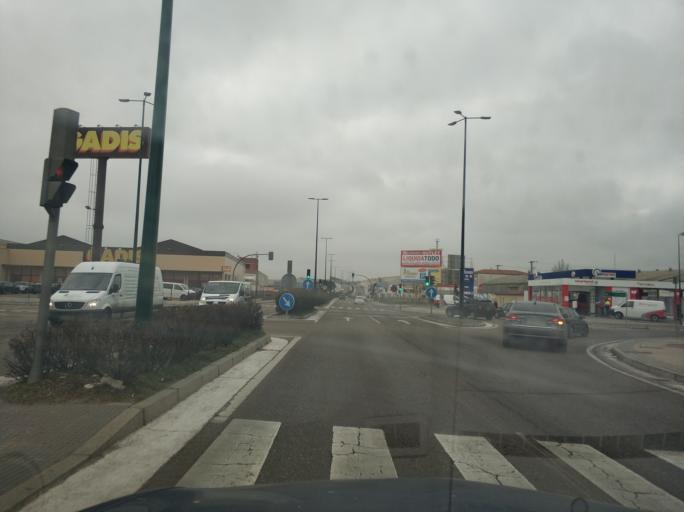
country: ES
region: Castille and Leon
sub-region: Provincia de Valladolid
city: Valladolid
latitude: 41.6190
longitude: -4.7350
